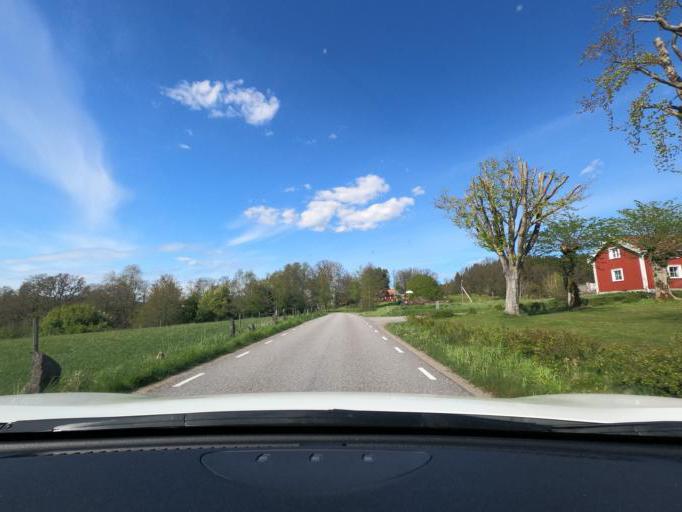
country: SE
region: Vaestra Goetaland
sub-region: Harryda Kommun
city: Ravlanda
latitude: 57.6245
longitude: 12.4982
